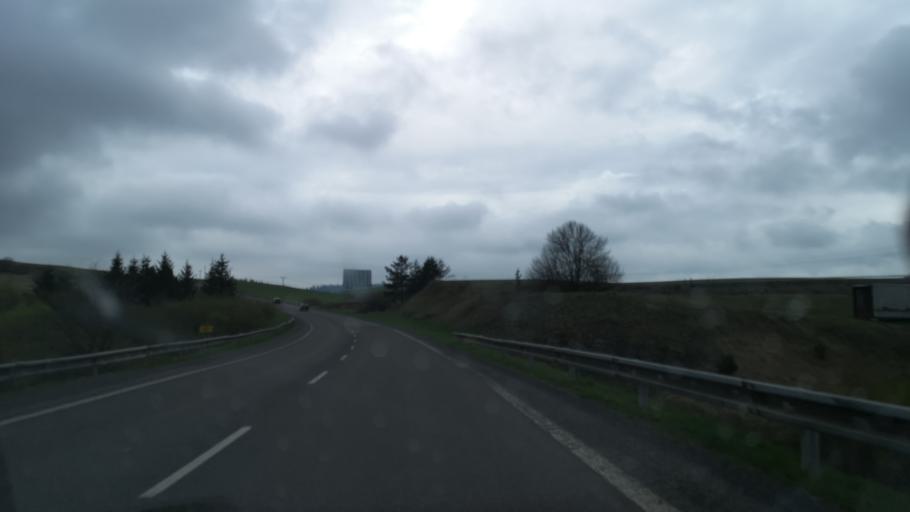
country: SK
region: Presovsky
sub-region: Okres Poprad
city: Strba
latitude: 49.0626
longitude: 19.9649
